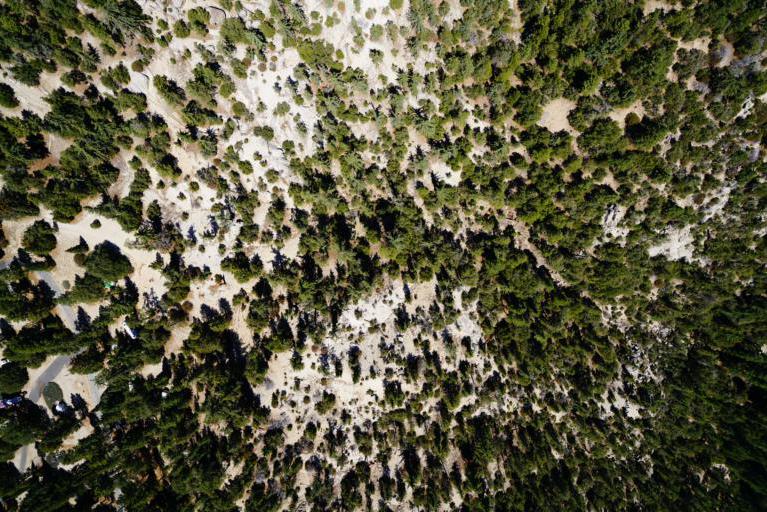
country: US
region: California
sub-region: Riverside County
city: Idyllwild-Pine Cove
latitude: 33.7707
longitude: -116.7230
